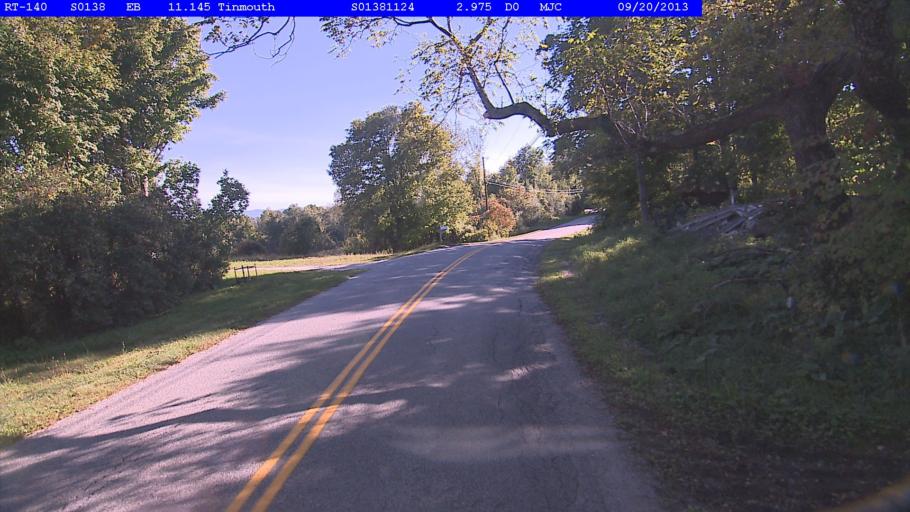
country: US
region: Vermont
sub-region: Rutland County
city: West Rutland
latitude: 43.4527
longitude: -73.0493
